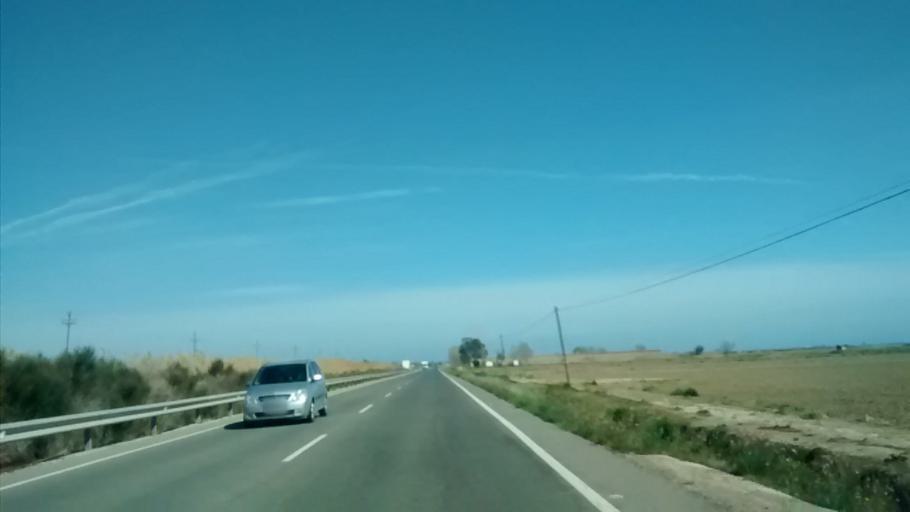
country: ES
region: Catalonia
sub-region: Provincia de Tarragona
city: Deltebre
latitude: 40.7053
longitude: 0.7806
